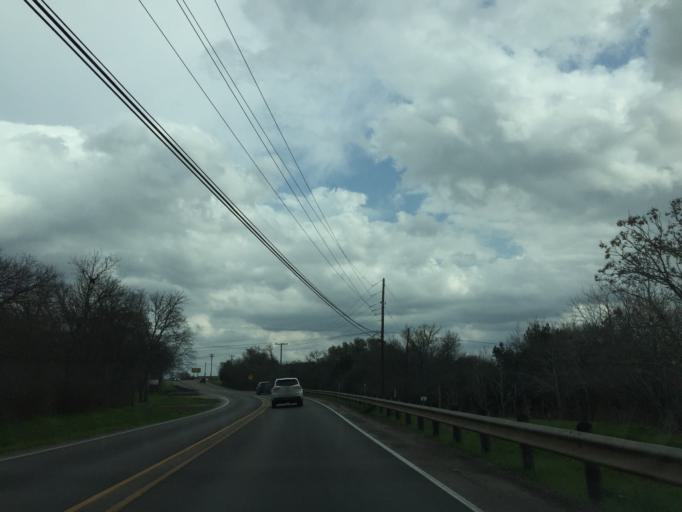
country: US
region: Texas
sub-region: Travis County
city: Manchaca
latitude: 30.1418
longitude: -97.8412
